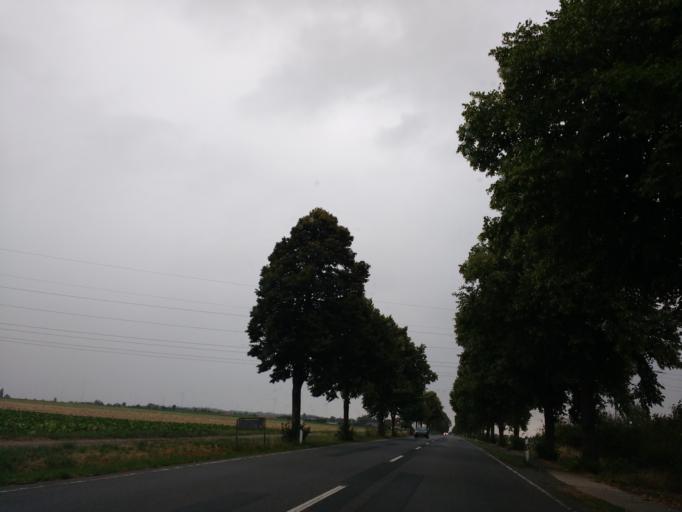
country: DE
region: Lower Saxony
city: Sohlde
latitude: 52.2223
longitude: 10.2247
